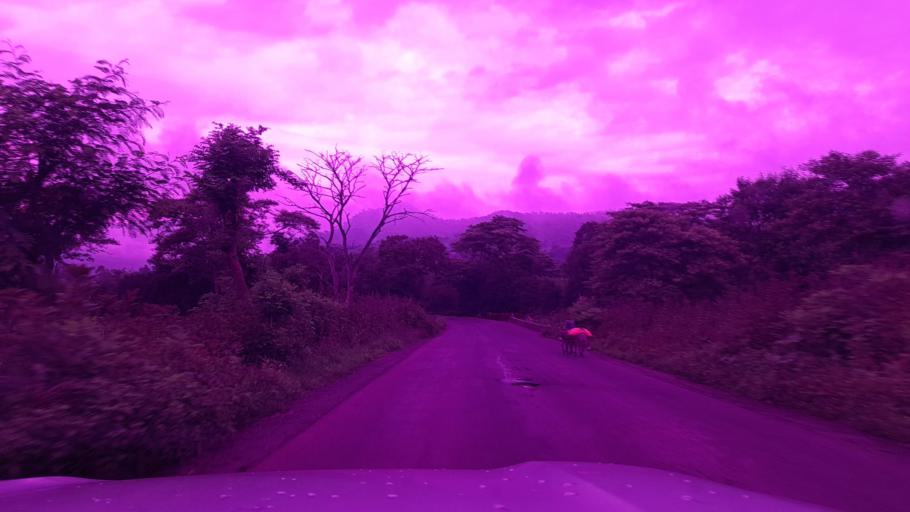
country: ET
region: Oromiya
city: Waliso
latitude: 8.2244
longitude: 37.5736
